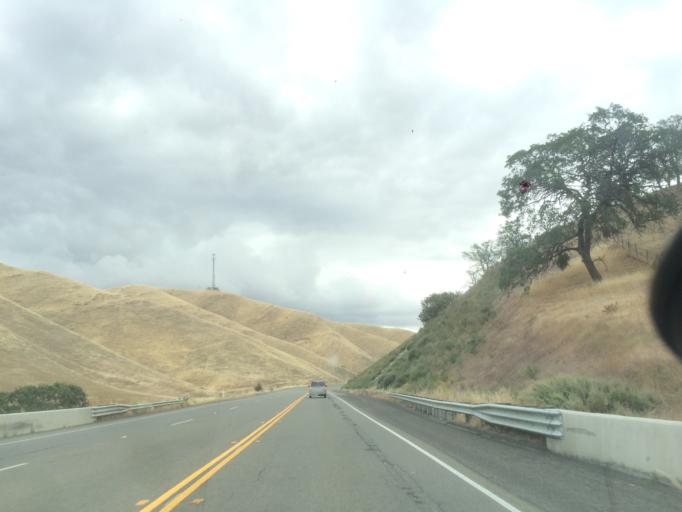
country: US
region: California
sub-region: San Luis Obispo County
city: Shandon
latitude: 35.7775
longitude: -120.1886
